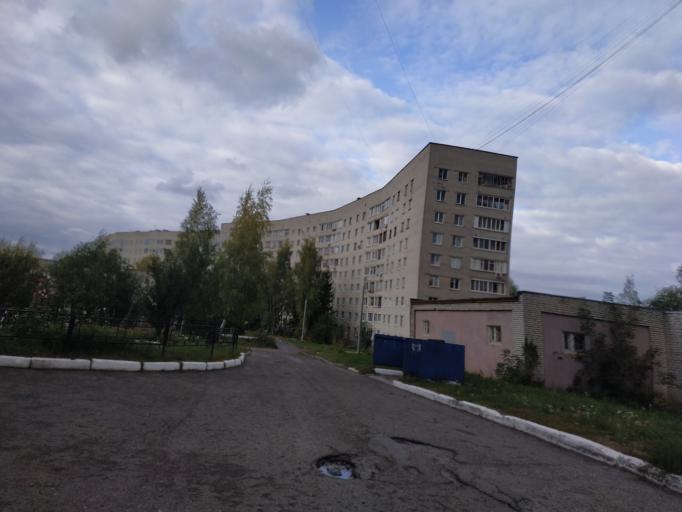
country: RU
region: Chuvashia
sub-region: Cheboksarskiy Rayon
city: Cheboksary
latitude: 56.1467
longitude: 47.2170
